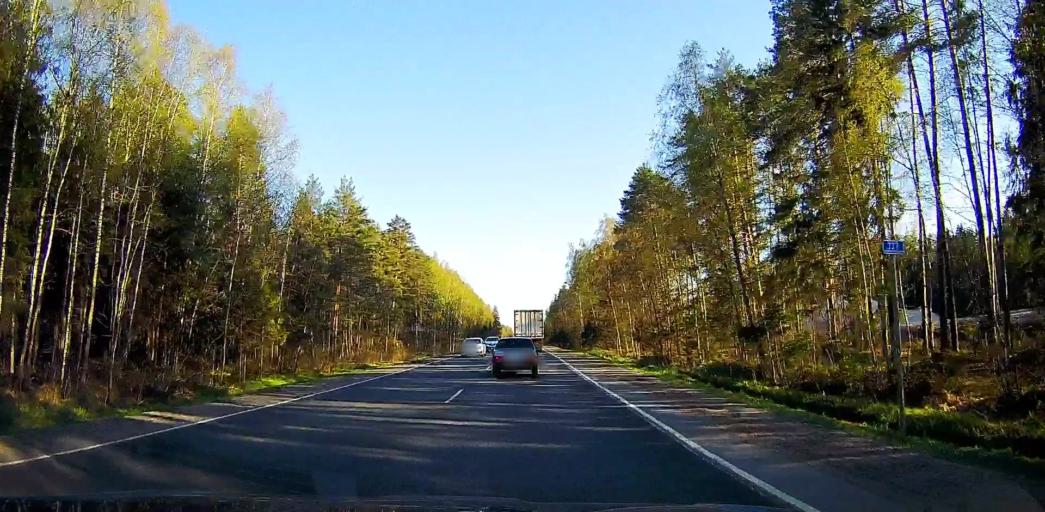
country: RU
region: Moskovskaya
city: Gzhel'
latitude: 55.5579
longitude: 38.3977
